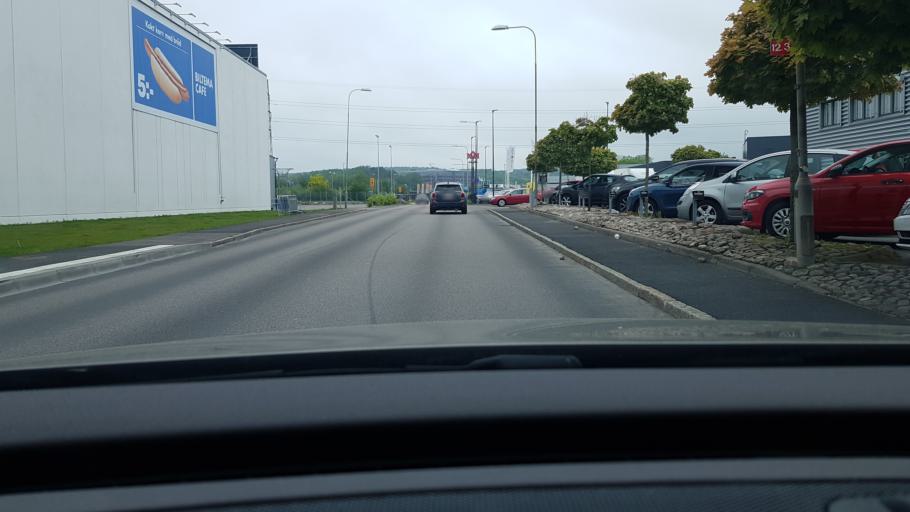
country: SE
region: Vaestra Goetaland
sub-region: Molndal
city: Moelndal
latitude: 57.6436
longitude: 11.9556
